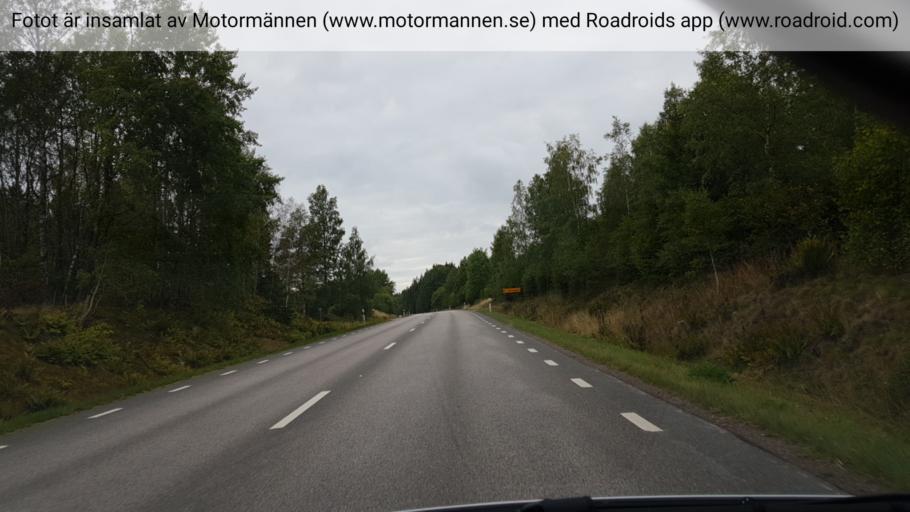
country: SE
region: Vaestra Goetaland
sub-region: Tibro Kommun
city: Tibro
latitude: 58.3420
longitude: 14.1821
